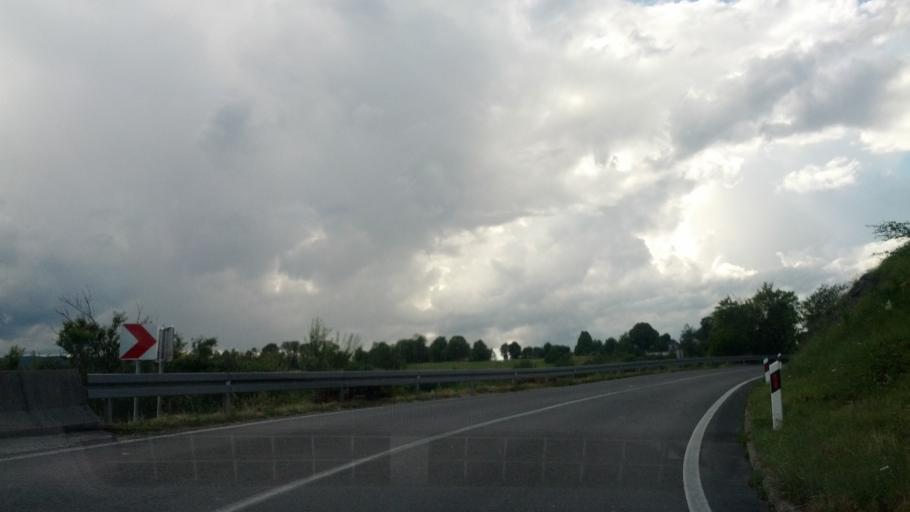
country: BA
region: Federation of Bosnia and Herzegovina
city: Izacic
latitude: 44.8755
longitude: 15.7800
